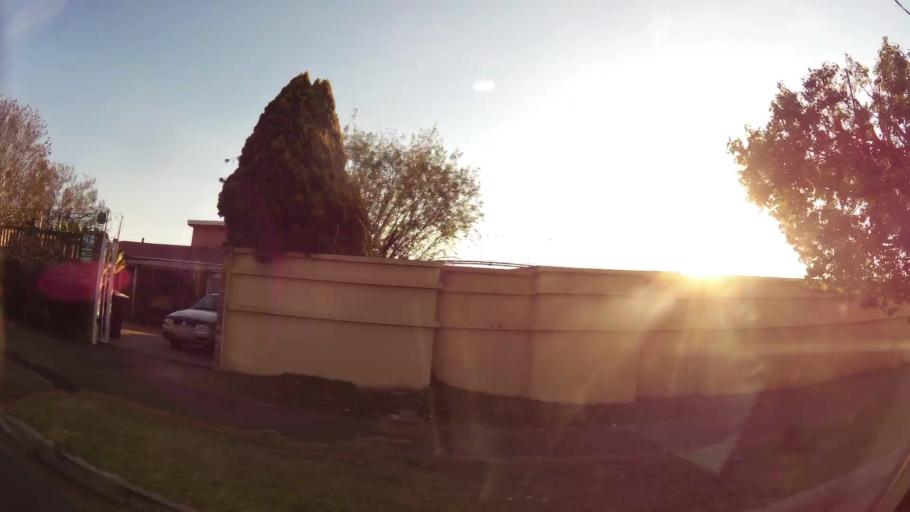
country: ZA
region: Gauteng
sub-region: City of Johannesburg Metropolitan Municipality
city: Johannesburg
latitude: -26.2537
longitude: 28.0072
